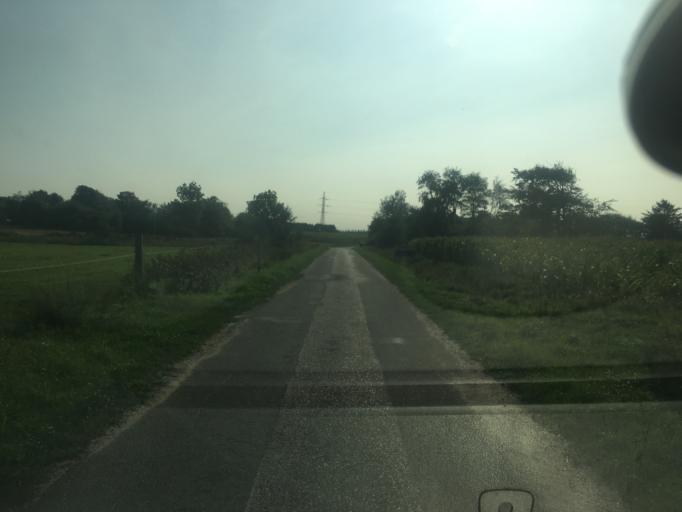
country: DK
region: South Denmark
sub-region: Tonder Kommune
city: Tonder
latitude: 54.9616
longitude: 8.9004
